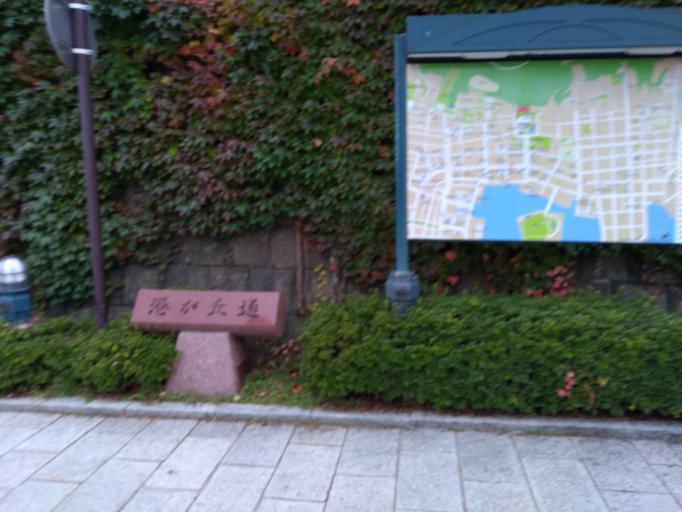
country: JP
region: Hokkaido
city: Hakodate
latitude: 41.7648
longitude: 140.7098
